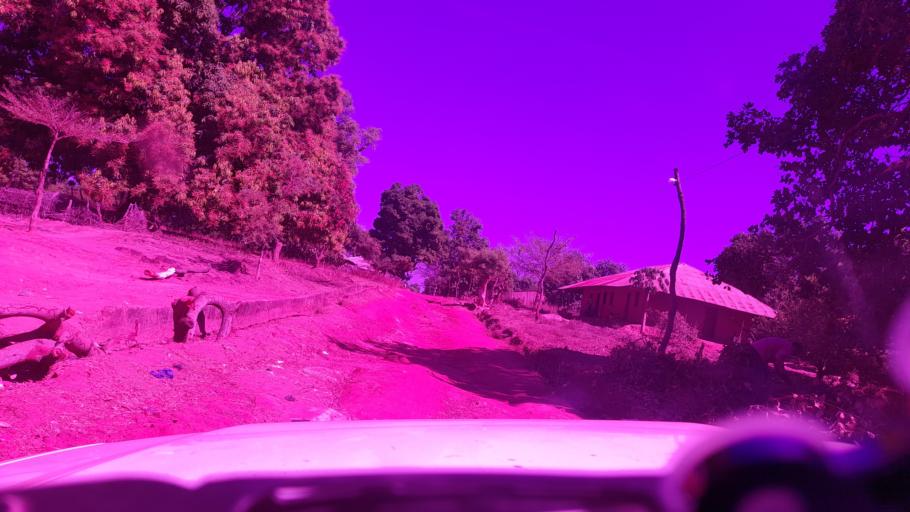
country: GW
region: Oio
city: Bissora
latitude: 12.4390
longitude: -15.5409
